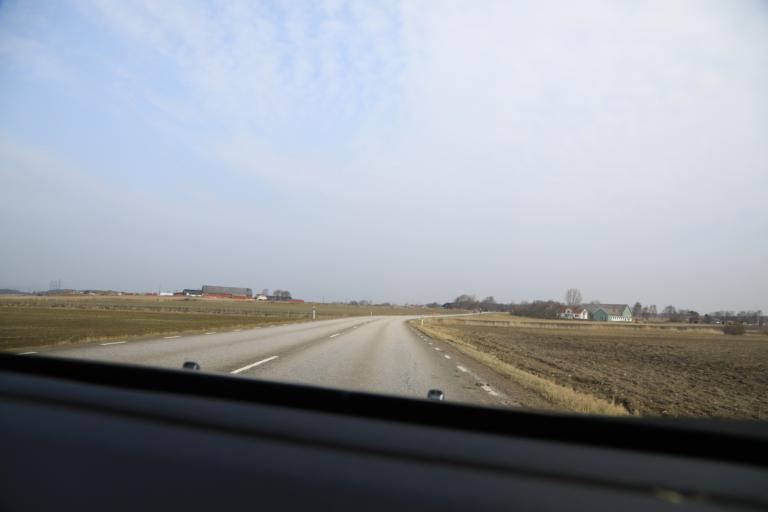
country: SE
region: Halland
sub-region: Kungsbacka Kommun
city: Frillesas
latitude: 57.2630
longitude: 12.1790
